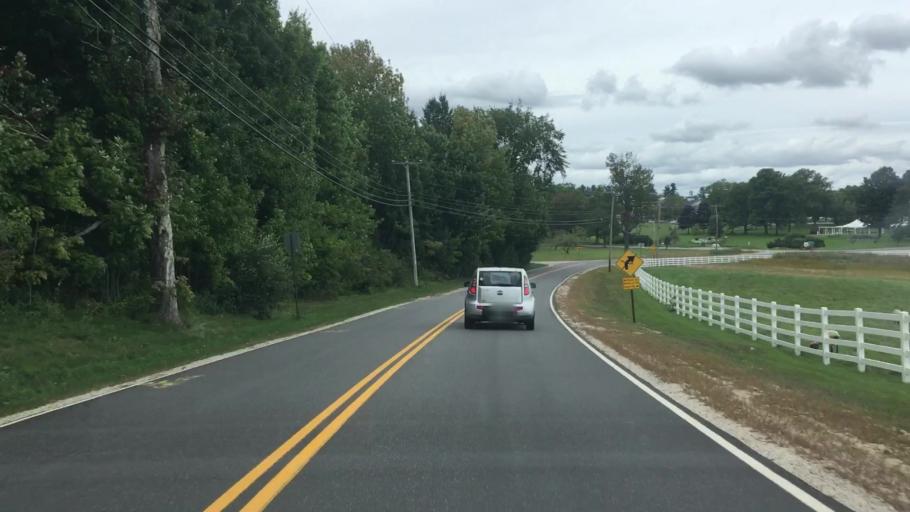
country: US
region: Maine
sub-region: Cumberland County
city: New Gloucester
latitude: 43.8978
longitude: -70.2564
